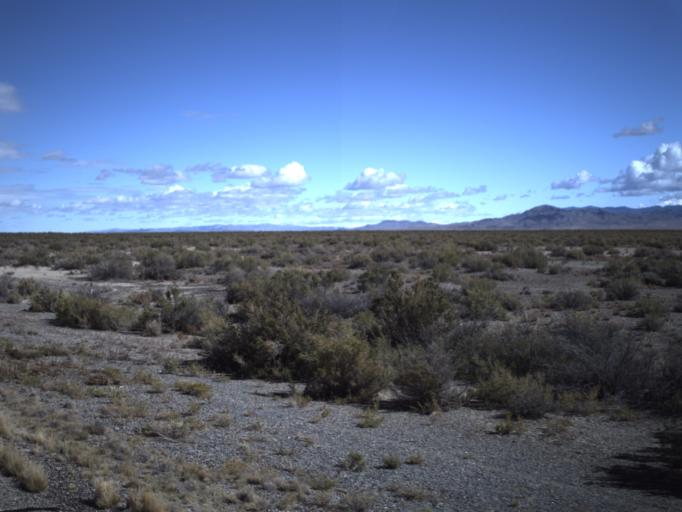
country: US
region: Nevada
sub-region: White Pine County
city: McGill
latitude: 39.0327
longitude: -114.0358
